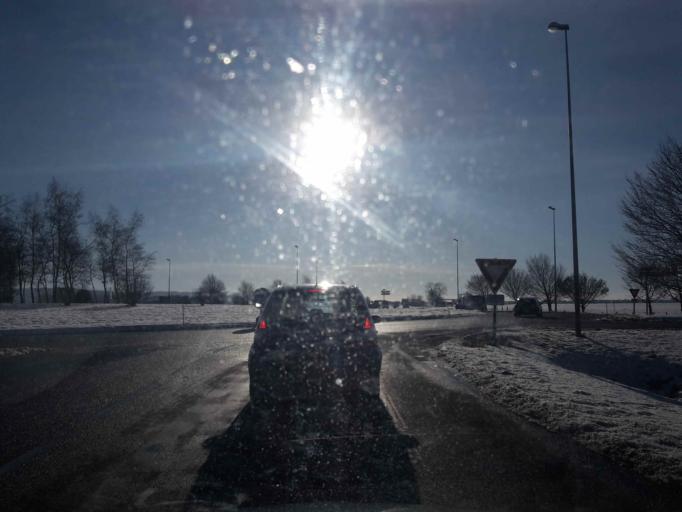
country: FR
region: Franche-Comte
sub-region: Departement du Doubs
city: Doubs
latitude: 46.9252
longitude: 6.3377
